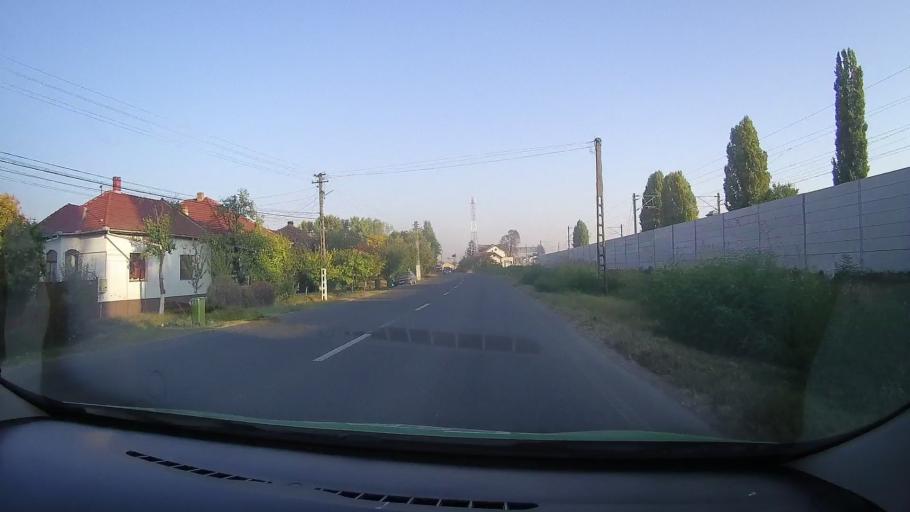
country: RO
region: Arad
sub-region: Comuna Sofronea
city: Sofronea
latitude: 46.2751
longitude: 21.3147
